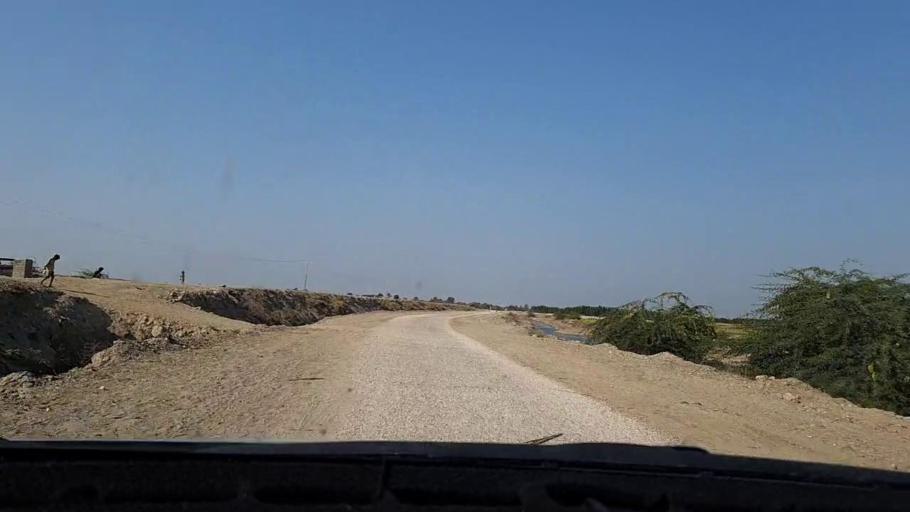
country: PK
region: Sindh
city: Tando Mittha Khan
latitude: 25.8216
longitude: 69.2931
